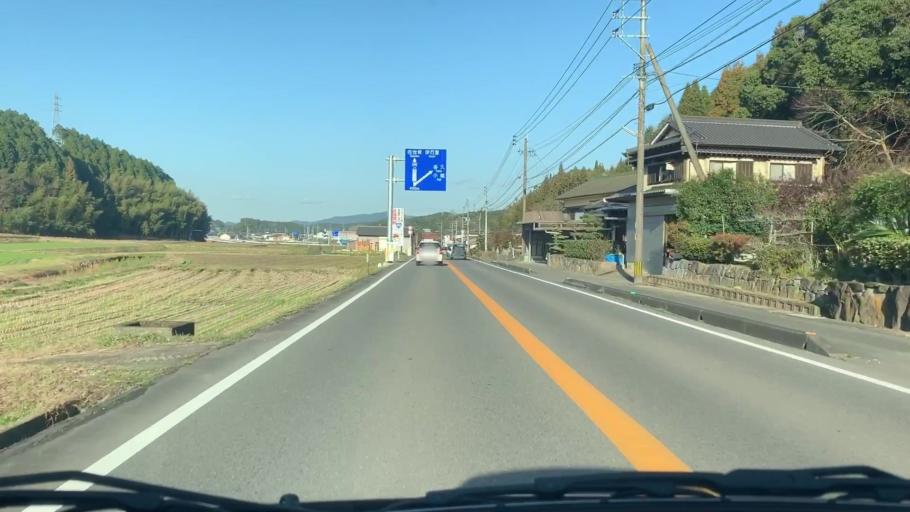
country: JP
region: Saga Prefecture
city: Takeocho-takeo
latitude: 33.2480
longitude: 130.0031
